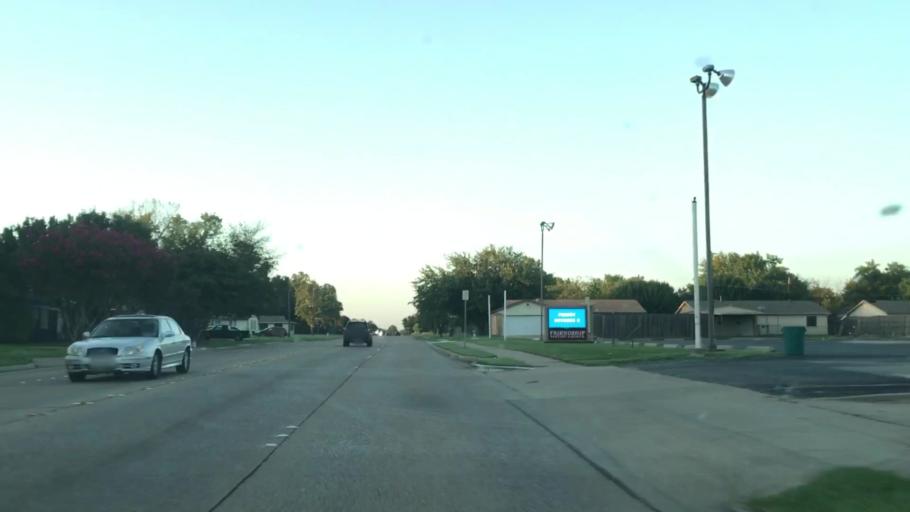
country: US
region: Texas
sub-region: Dallas County
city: Mesquite
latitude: 32.7561
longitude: -96.5835
